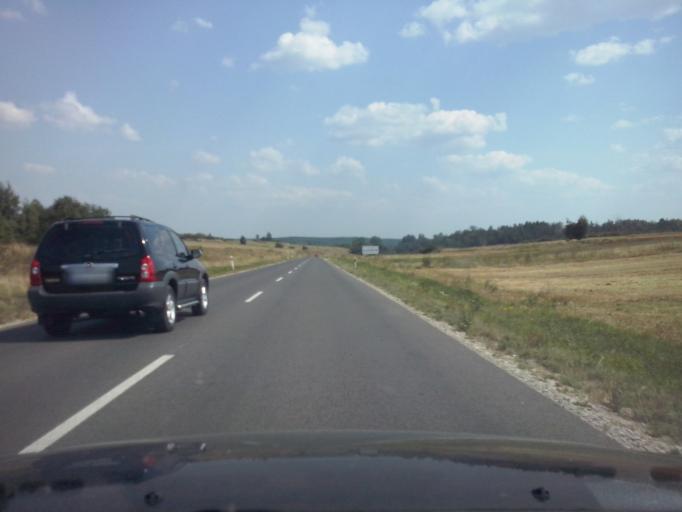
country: PL
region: Swietokrzyskie
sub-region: Powiat staszowski
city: Staszow
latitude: 50.5848
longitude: 21.0935
